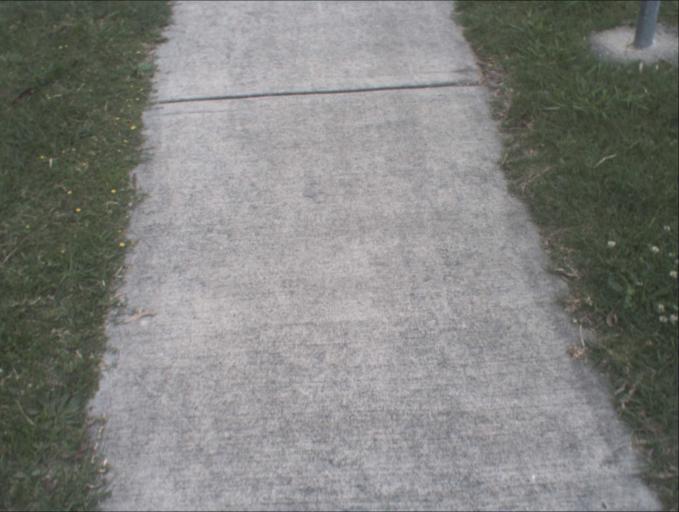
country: AU
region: Queensland
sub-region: Logan
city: Park Ridge South
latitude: -27.6966
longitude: 153.0366
